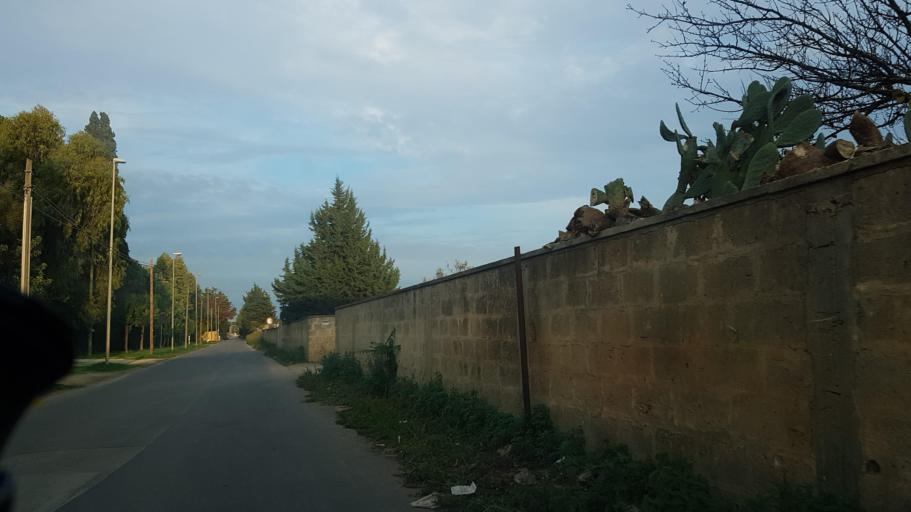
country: IT
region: Apulia
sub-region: Provincia di Brindisi
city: Latiano
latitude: 40.5547
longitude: 17.7245
